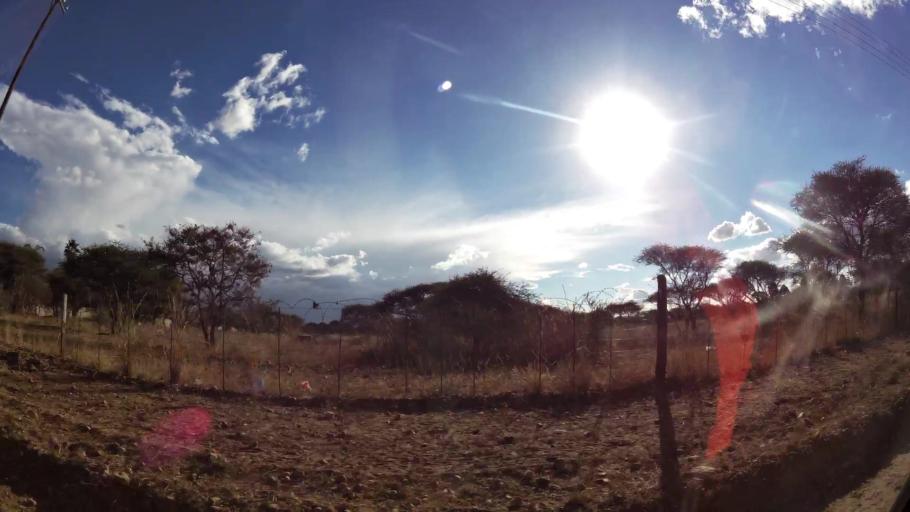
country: ZA
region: Limpopo
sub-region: Capricorn District Municipality
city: Polokwane
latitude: -23.9319
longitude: 29.4451
